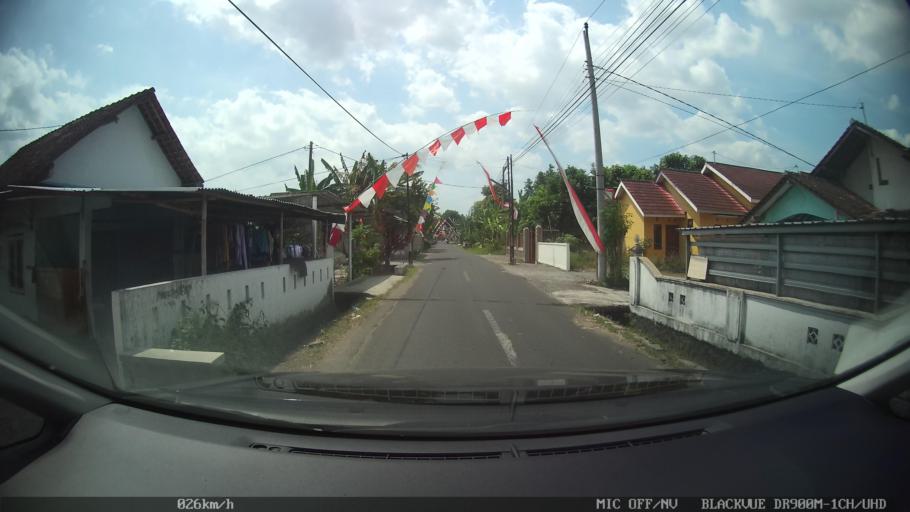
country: ID
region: Daerah Istimewa Yogyakarta
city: Kasihan
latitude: -7.8123
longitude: 110.3403
